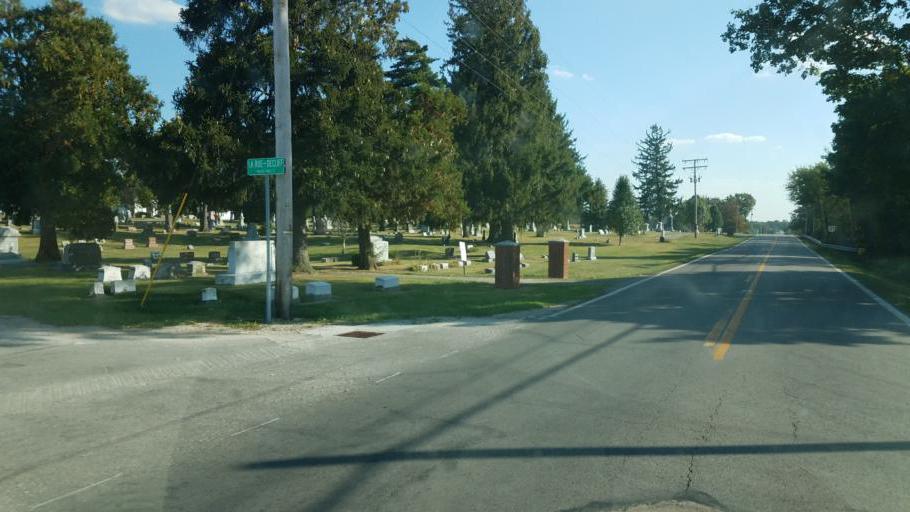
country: US
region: Ohio
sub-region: Union County
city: Richwood
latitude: 40.6002
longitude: -83.3805
